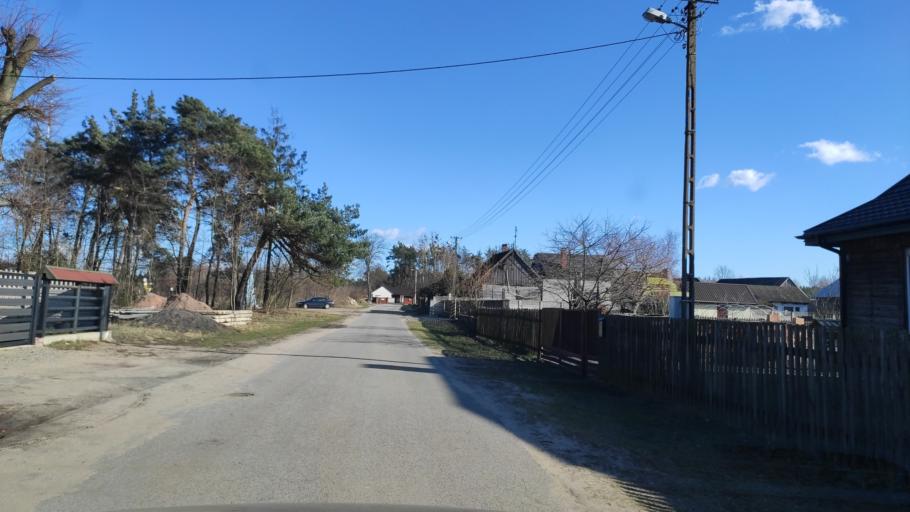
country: PL
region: Masovian Voivodeship
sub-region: Powiat radomski
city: Jastrzebia
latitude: 51.4561
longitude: 21.2704
